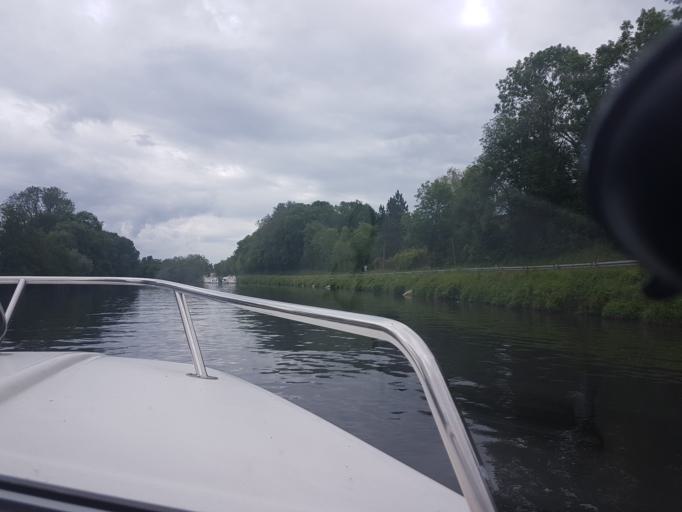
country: FR
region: Bourgogne
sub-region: Departement de l'Yonne
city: Champs-sur-Yonne
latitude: 47.7430
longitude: 3.5879
